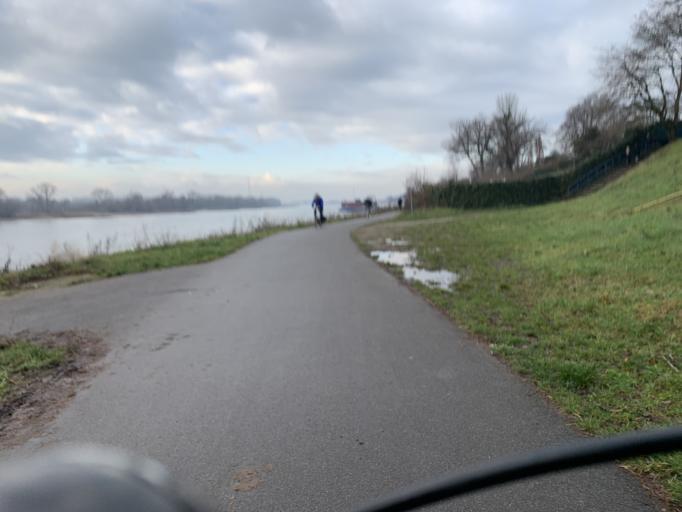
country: DE
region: North Rhine-Westphalia
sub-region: Regierungsbezirk Dusseldorf
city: Meerbusch
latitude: 51.3235
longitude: 6.7343
